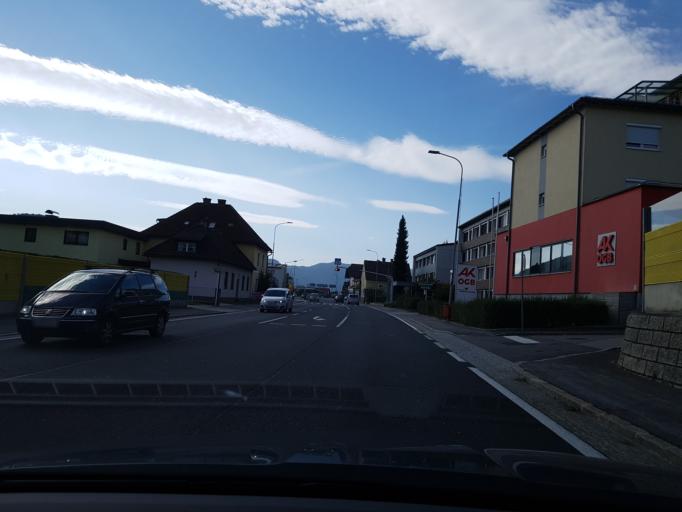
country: AT
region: Carinthia
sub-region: Politischer Bezirk Feldkirchen
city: Feldkirchen in Karnten
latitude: 46.7290
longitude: 14.0913
